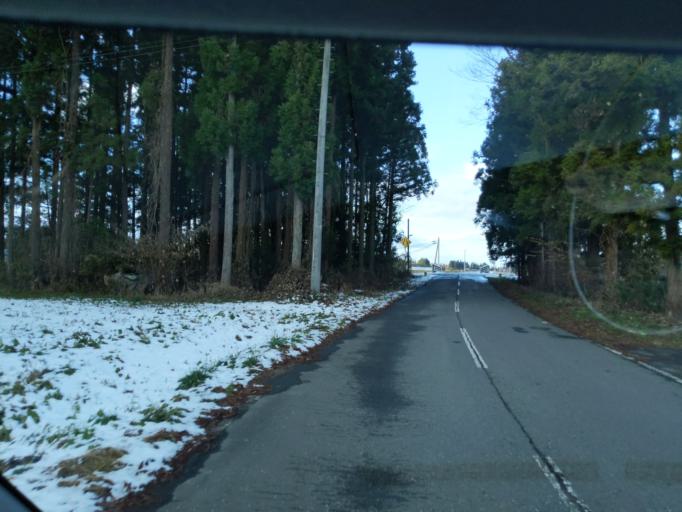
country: JP
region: Iwate
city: Kitakami
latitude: 39.2126
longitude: 141.0493
